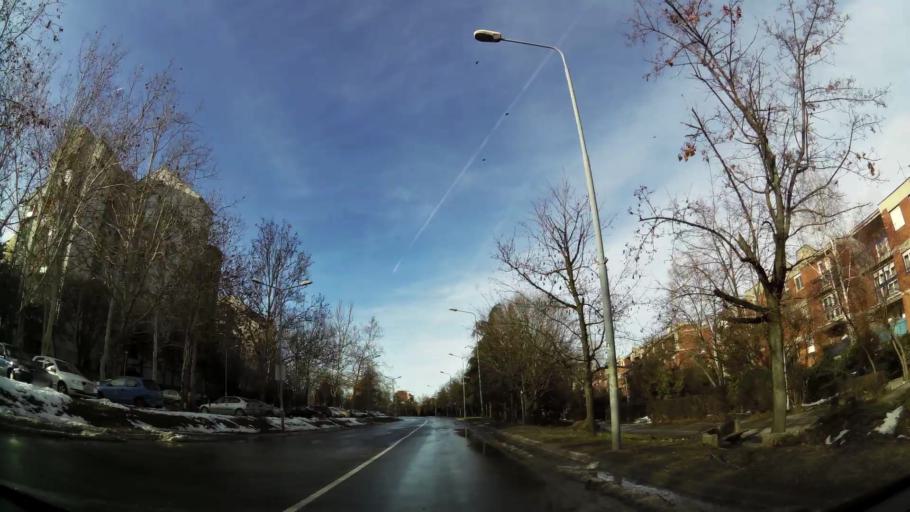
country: RS
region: Central Serbia
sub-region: Belgrade
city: Rakovica
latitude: 44.7285
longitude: 20.4255
